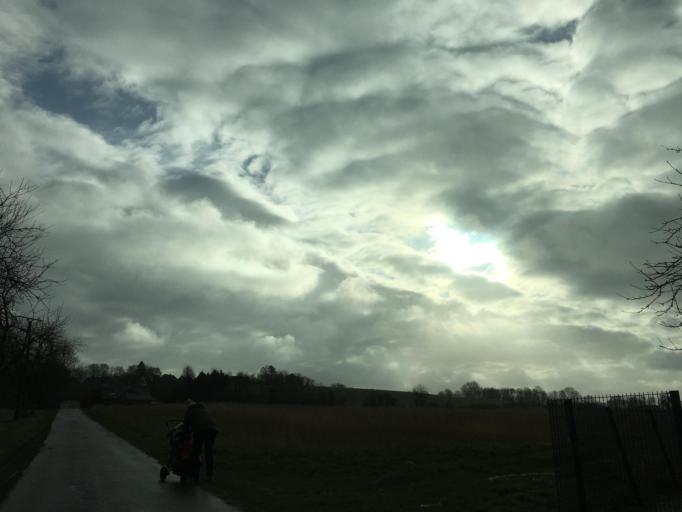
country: DE
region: North Rhine-Westphalia
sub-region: Regierungsbezirk Munster
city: Altenberge
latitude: 52.0485
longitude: 7.4511
